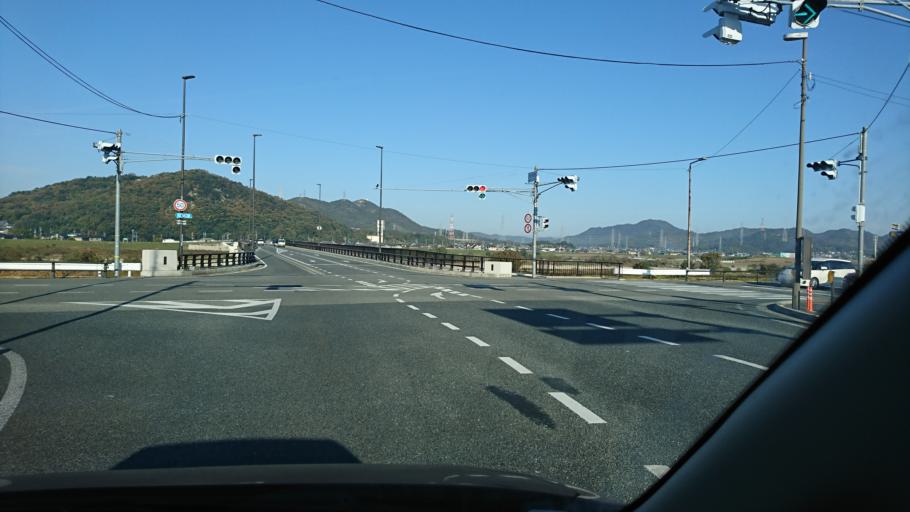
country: JP
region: Hyogo
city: Kakogawacho-honmachi
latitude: 34.7880
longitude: 134.8683
